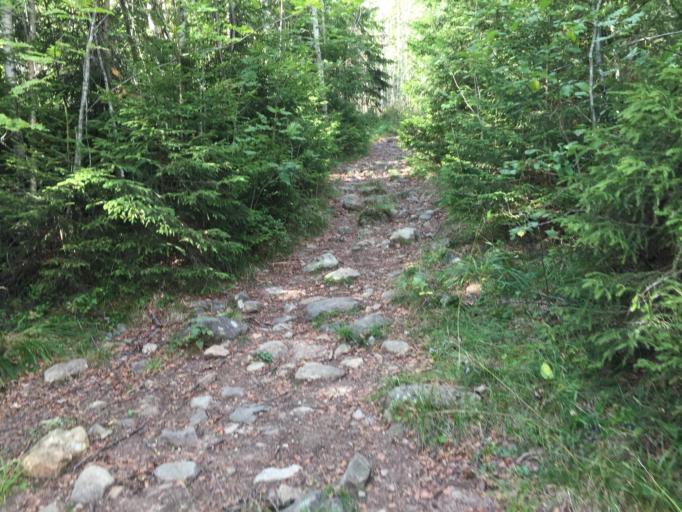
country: NO
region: Akershus
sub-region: Raelingen
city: Fjerdingby
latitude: 59.9114
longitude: 11.0288
